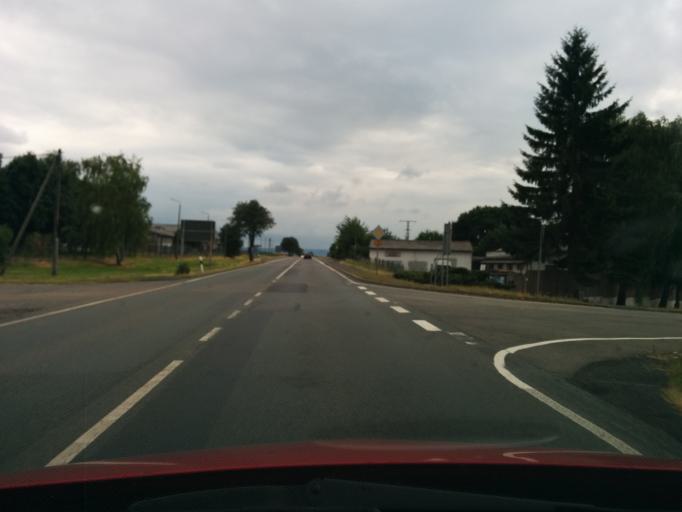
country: DE
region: Thuringia
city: Henschleben
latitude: 51.1420
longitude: 10.9727
